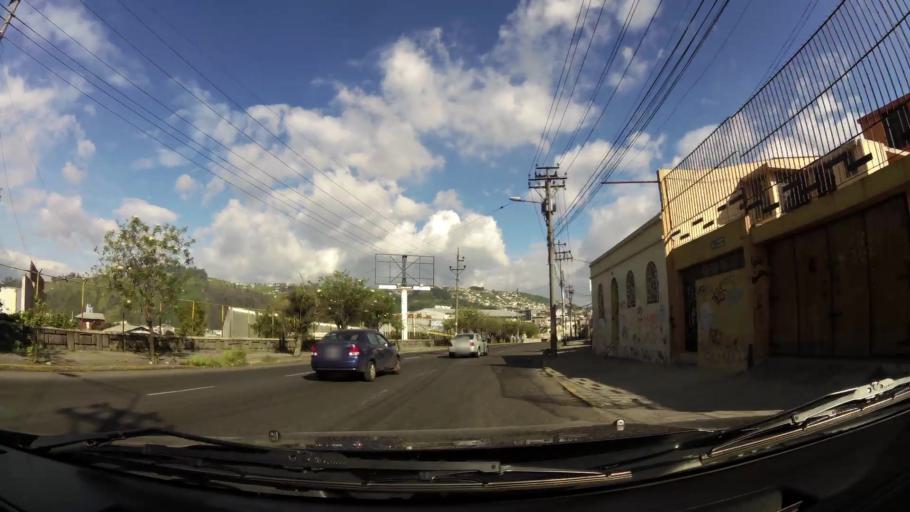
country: EC
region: Pichincha
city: Quito
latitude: -0.2139
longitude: -78.4914
